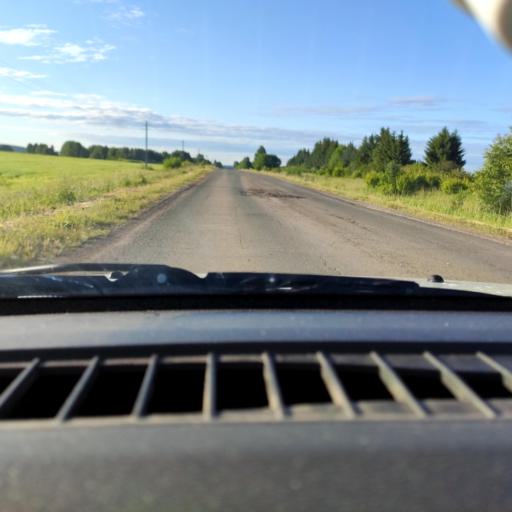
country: RU
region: Perm
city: Uinskoye
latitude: 57.1016
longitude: 56.5400
